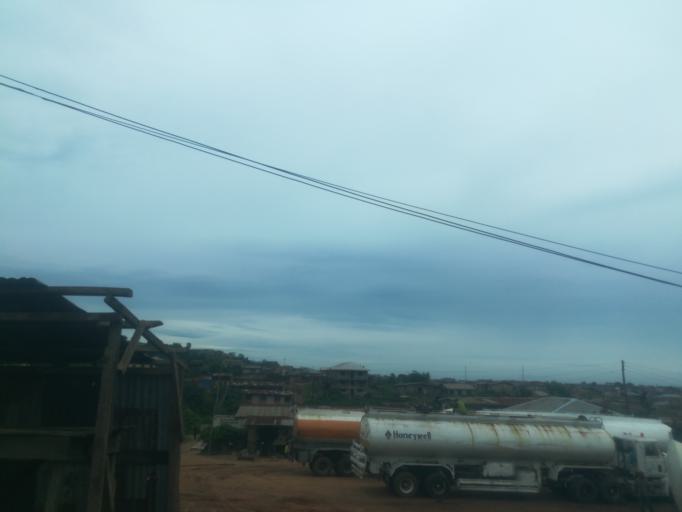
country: NG
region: Oyo
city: Ibadan
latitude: 7.3431
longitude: 3.9126
